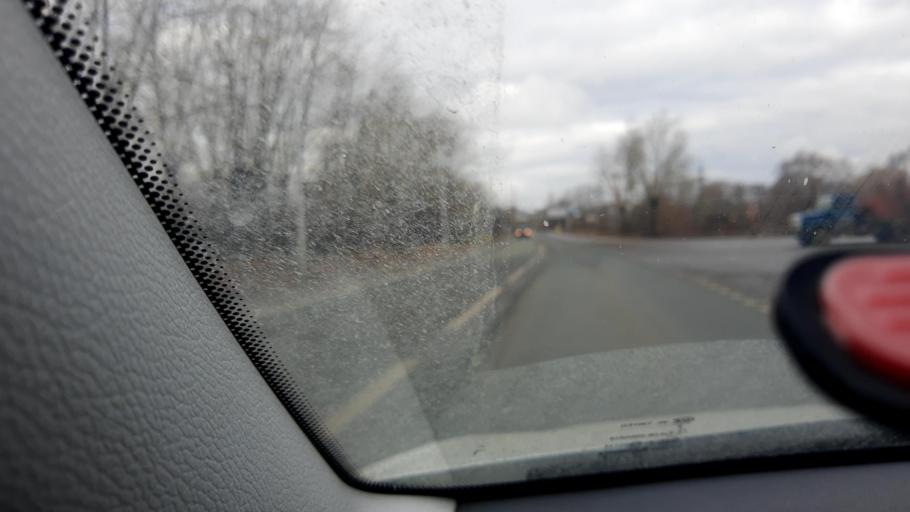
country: RU
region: Bashkortostan
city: Ufa
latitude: 54.8606
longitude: 56.1121
